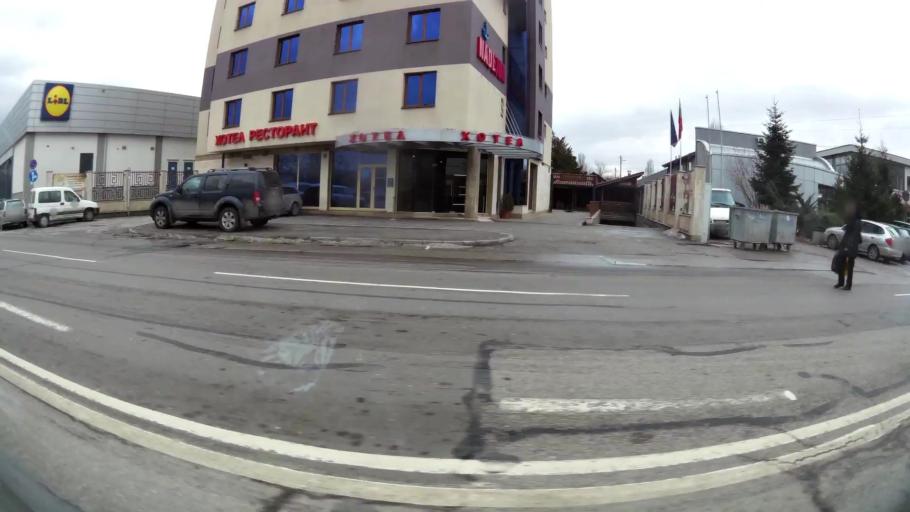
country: BG
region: Sofia-Capital
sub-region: Stolichna Obshtina
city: Sofia
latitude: 42.7319
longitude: 23.2851
